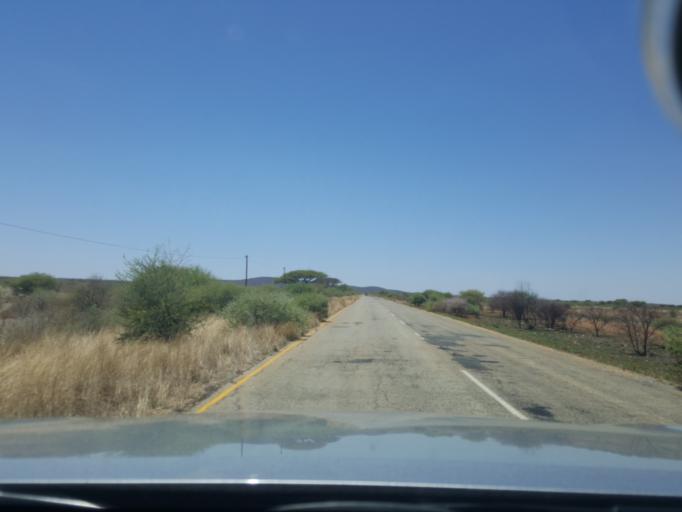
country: BW
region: South East
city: Ramotswa
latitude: -25.0712
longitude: 25.9482
